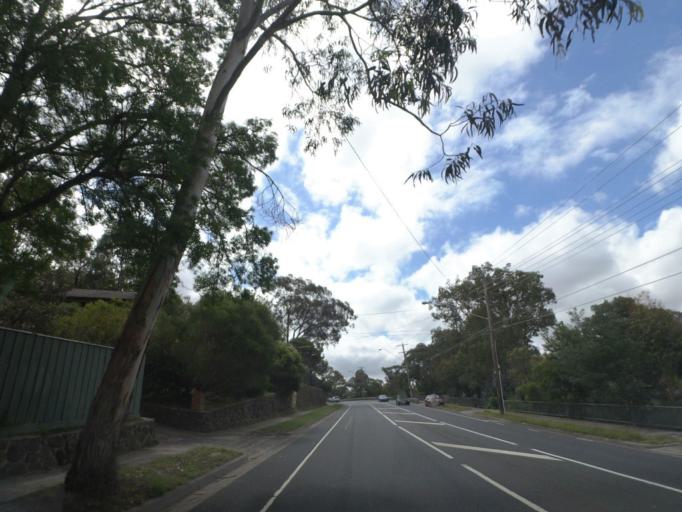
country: AU
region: Victoria
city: Saint Helena
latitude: -37.7067
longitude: 145.1308
